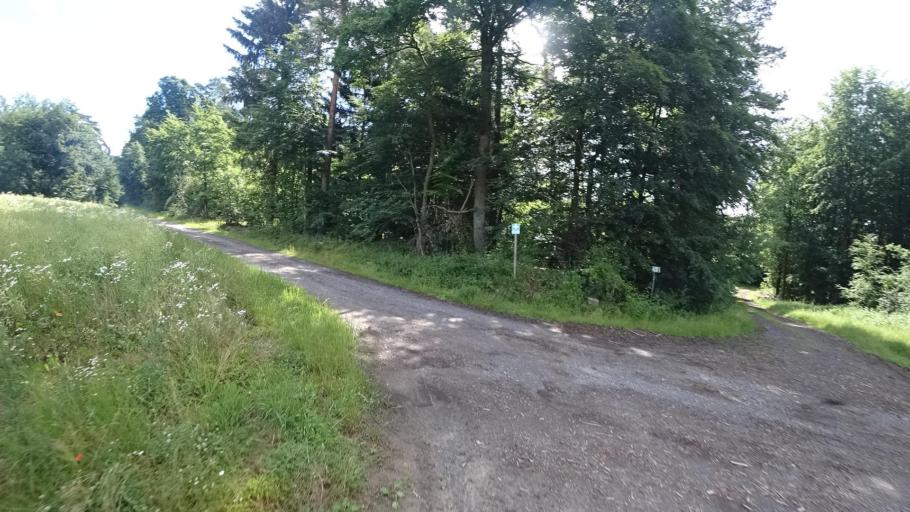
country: DE
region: Rheinland-Pfalz
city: Schoneberg
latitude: 50.6564
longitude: 7.5880
